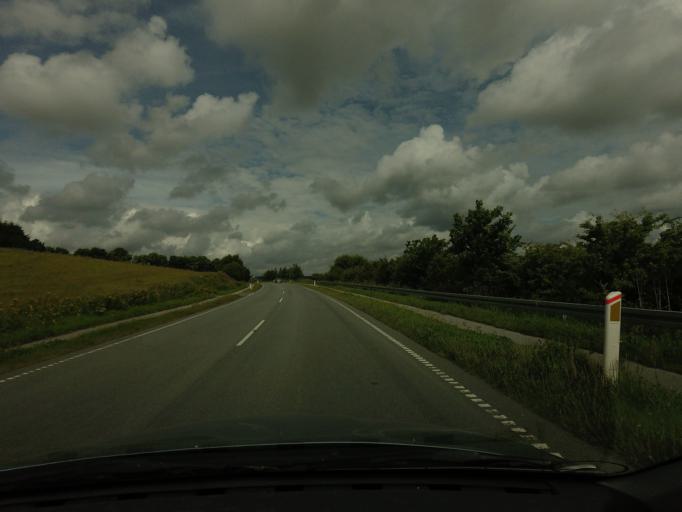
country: DK
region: North Denmark
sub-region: Hjorring Kommune
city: Tars
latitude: 57.3609
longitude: 10.2033
